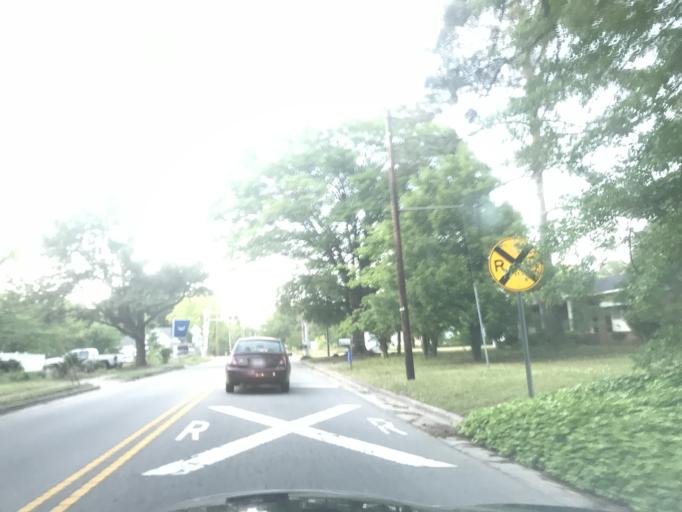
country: US
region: North Carolina
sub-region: Wake County
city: Wendell
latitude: 35.7818
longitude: -78.3744
